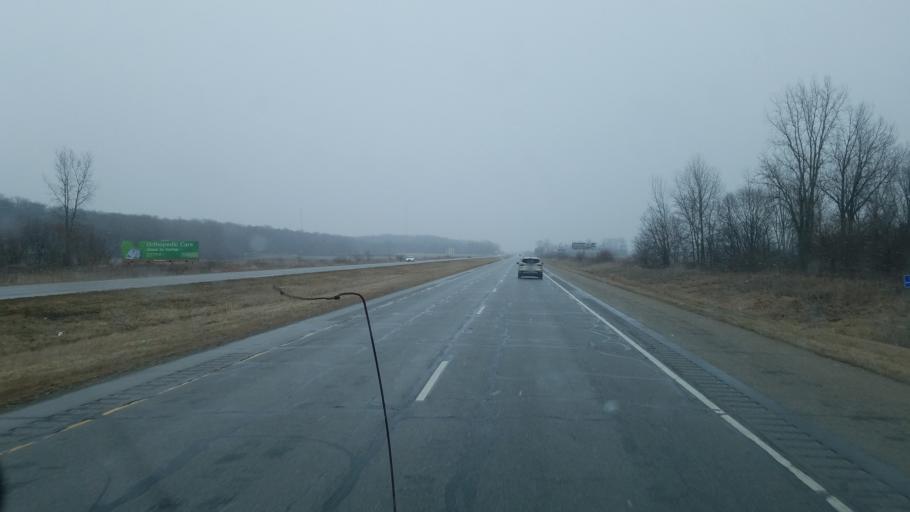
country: US
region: Indiana
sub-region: Miami County
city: Peru
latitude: 40.7728
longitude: -86.1138
